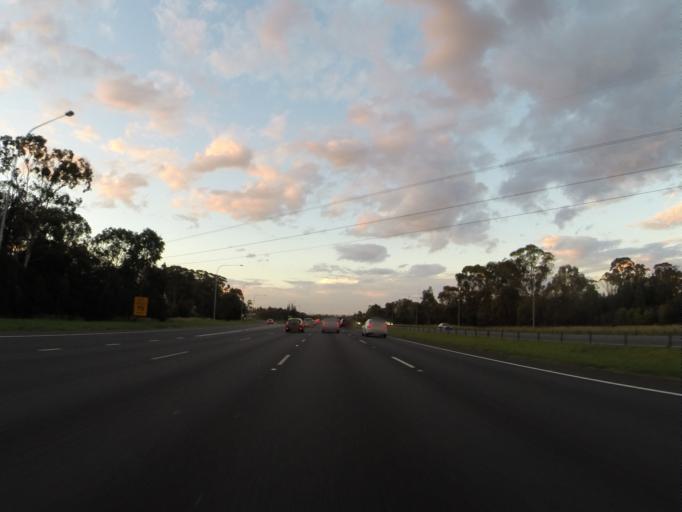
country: AU
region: New South Wales
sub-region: Campbelltown Municipality
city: Glenfield
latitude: -33.9612
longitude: 150.8757
